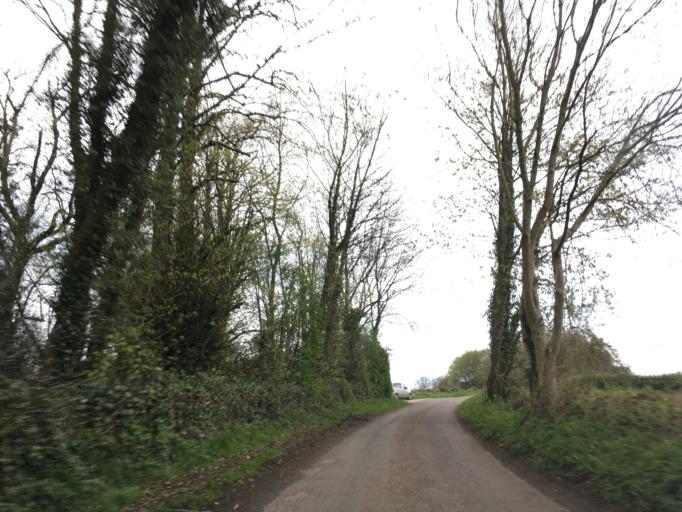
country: GB
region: England
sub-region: Gloucestershire
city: Wotton-under-Edge
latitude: 51.6499
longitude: -2.3034
